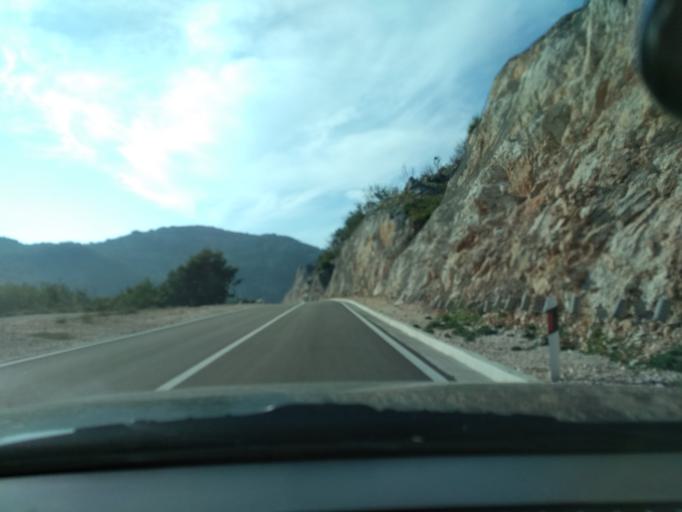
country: ME
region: Cetinje
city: Cetinje
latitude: 42.4256
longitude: 18.8706
